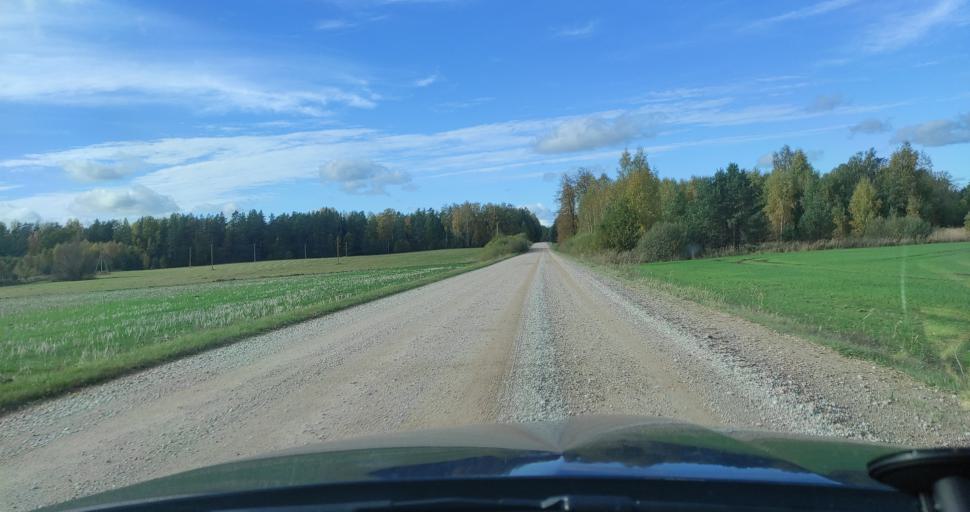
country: LV
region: Jaunpils
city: Jaunpils
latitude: 56.8292
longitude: 23.0143
